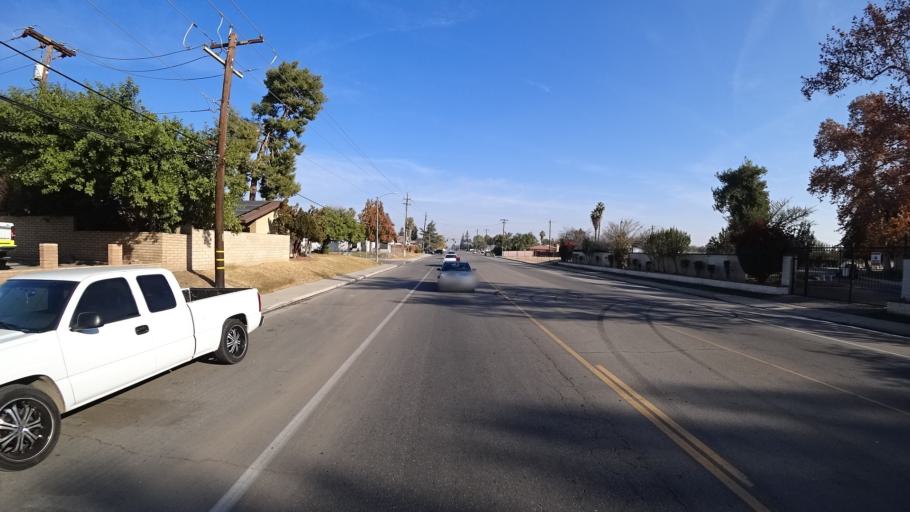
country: US
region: California
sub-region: Kern County
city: Bakersfield
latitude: 35.3250
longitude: -119.0457
